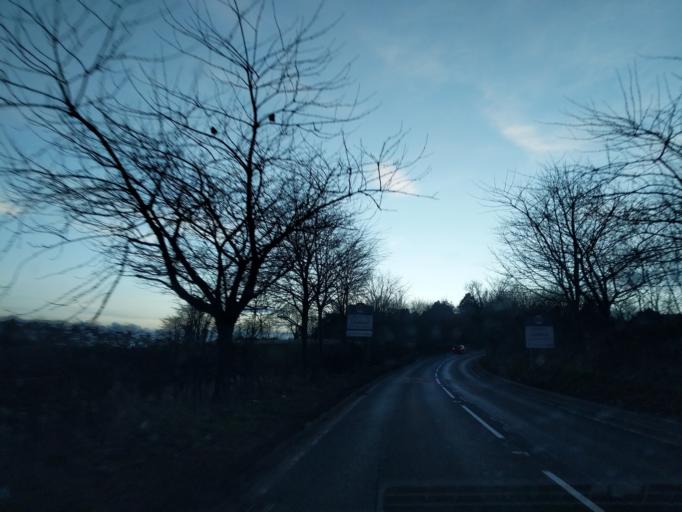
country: GB
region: Scotland
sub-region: Midlothian
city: Loanhead
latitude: 55.8792
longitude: -3.1361
